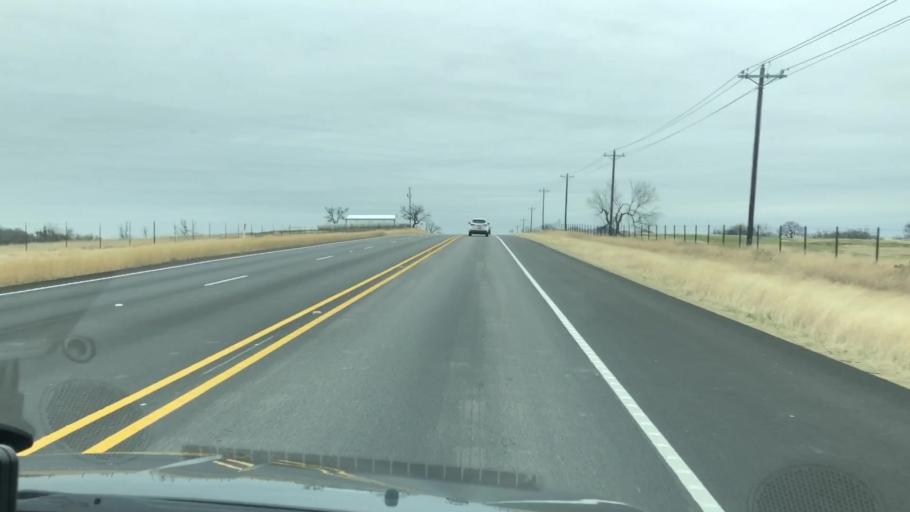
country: US
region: Texas
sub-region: Erath County
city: Stephenville
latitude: 32.2930
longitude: -98.1900
